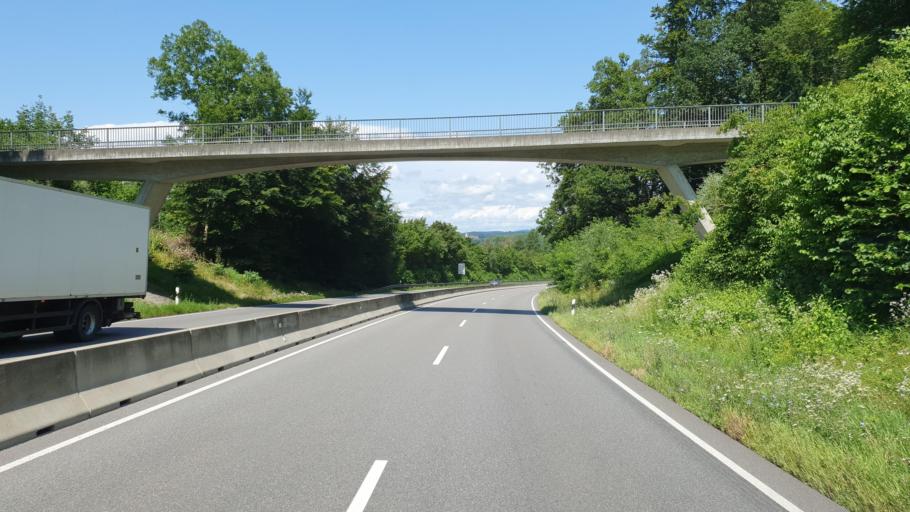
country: DE
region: Baden-Wuerttemberg
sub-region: Tuebingen Region
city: Uhldingen-Muhlhofen
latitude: 47.7228
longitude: 9.2383
